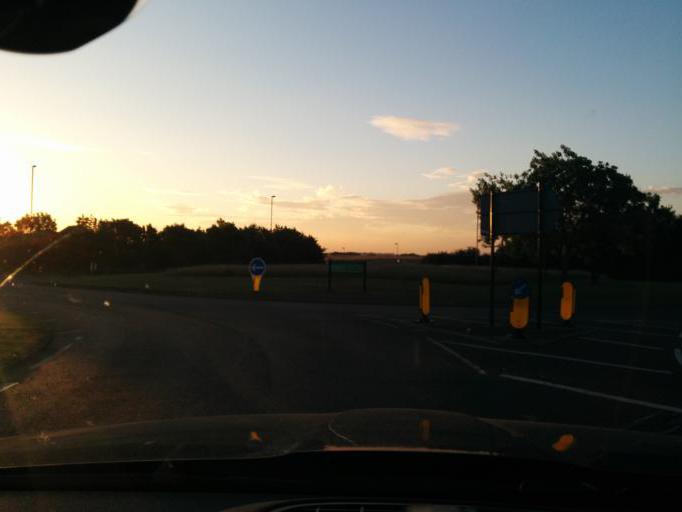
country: GB
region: England
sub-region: Northumberland
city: Seghill
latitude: 55.0418
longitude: -1.5645
